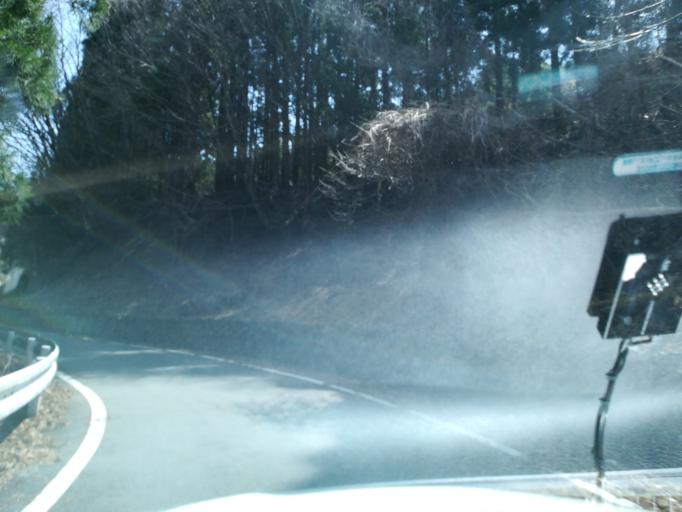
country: JP
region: Tokushima
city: Wakimachi
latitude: 33.8783
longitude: 134.0545
